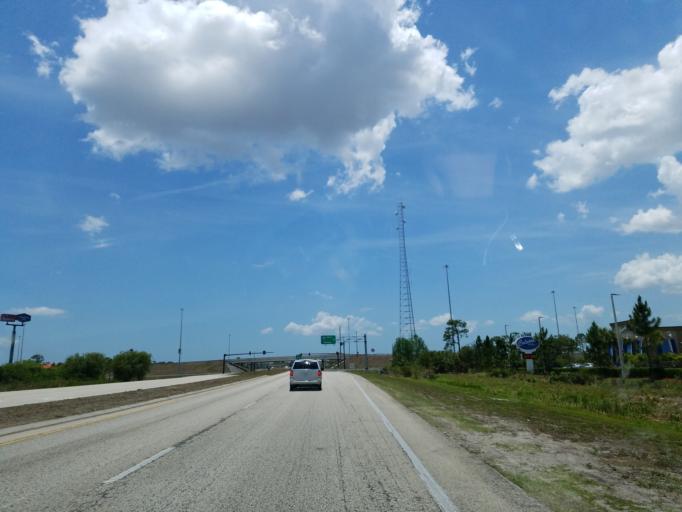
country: US
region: Florida
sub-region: Charlotte County
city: Harbour Heights
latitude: 27.0230
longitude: -82.0462
